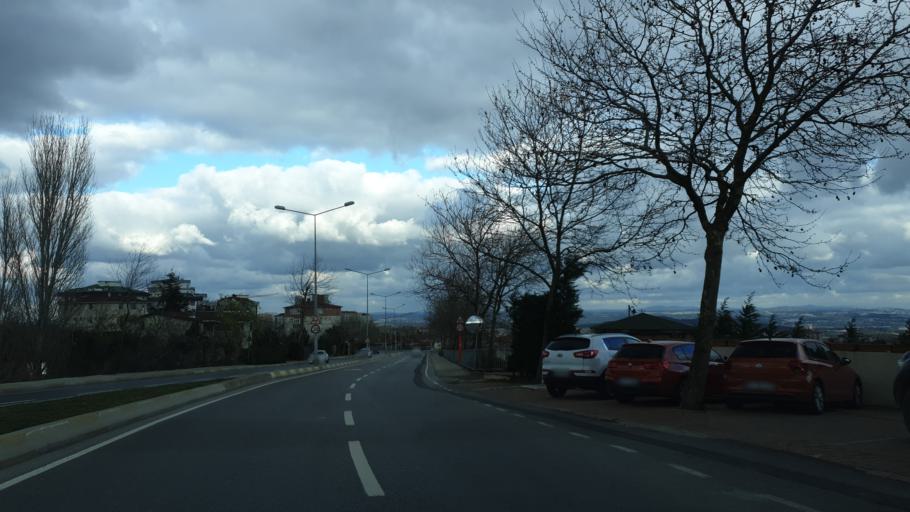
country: TR
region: Istanbul
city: Sultanbeyli
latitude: 40.9322
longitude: 29.2750
